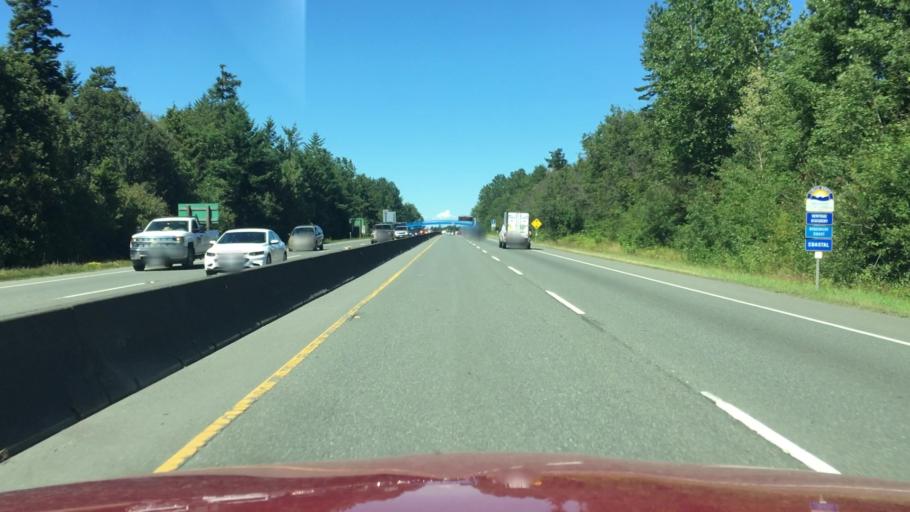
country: CA
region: British Columbia
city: North Saanich
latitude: 48.6374
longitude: -123.4088
